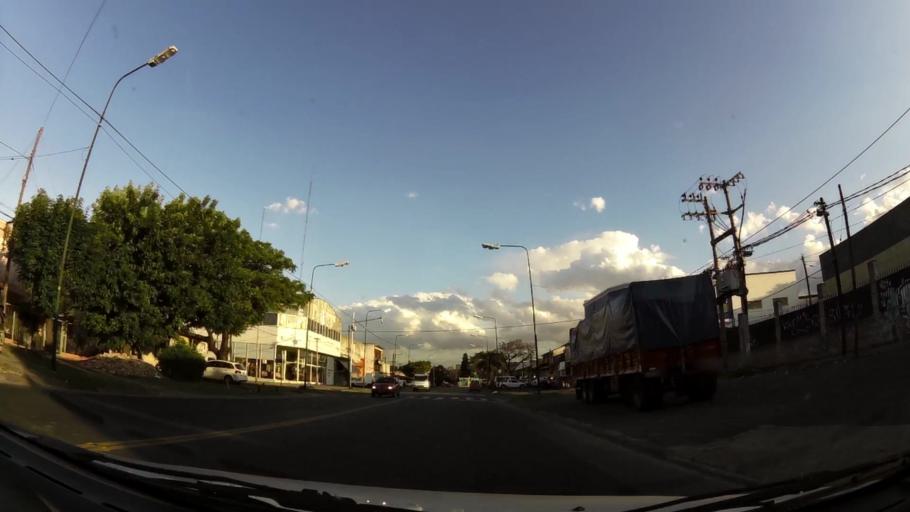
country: AR
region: Buenos Aires
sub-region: Partido de San Isidro
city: San Isidro
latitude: -34.4670
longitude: -58.5427
